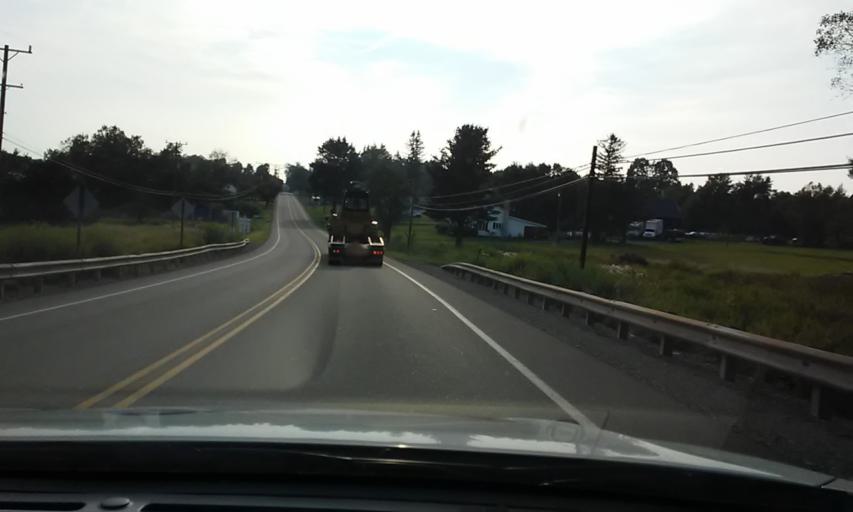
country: US
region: Pennsylvania
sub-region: McKean County
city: Kane
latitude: 41.7243
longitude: -78.6659
